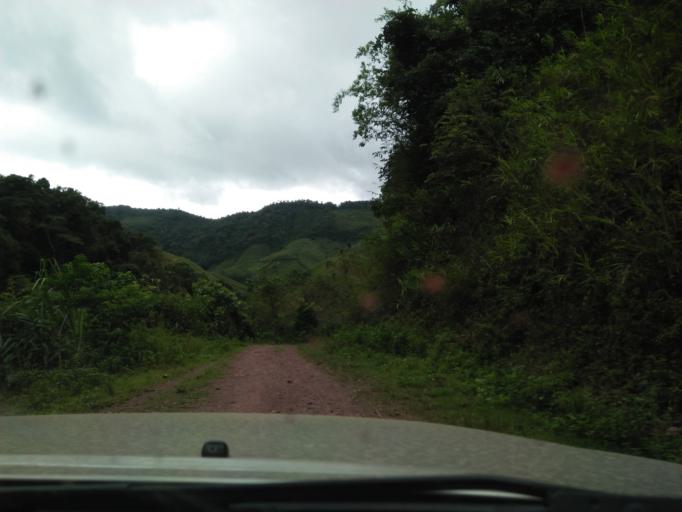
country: TH
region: Nan
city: Bo Kluea
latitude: 19.3795
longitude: 101.2142
